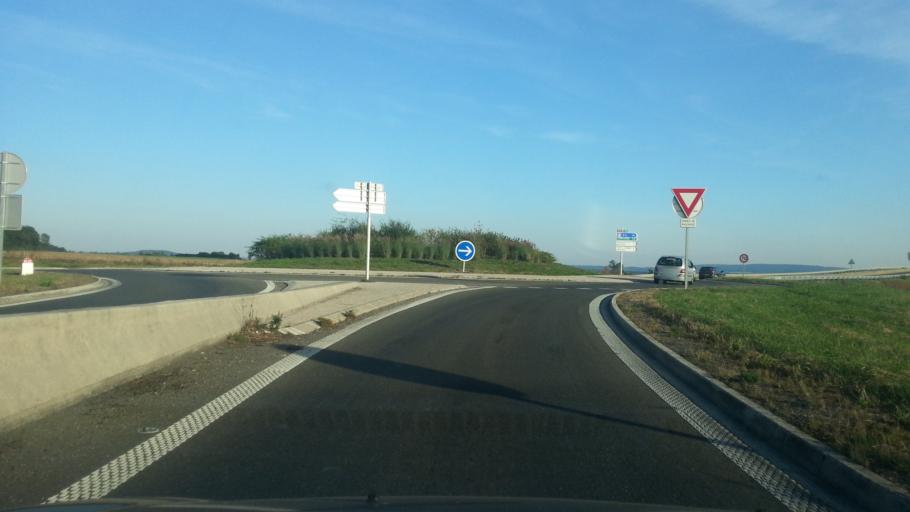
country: FR
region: Picardie
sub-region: Departement de l'Oise
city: Catenoy
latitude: 49.3793
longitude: 2.5224
